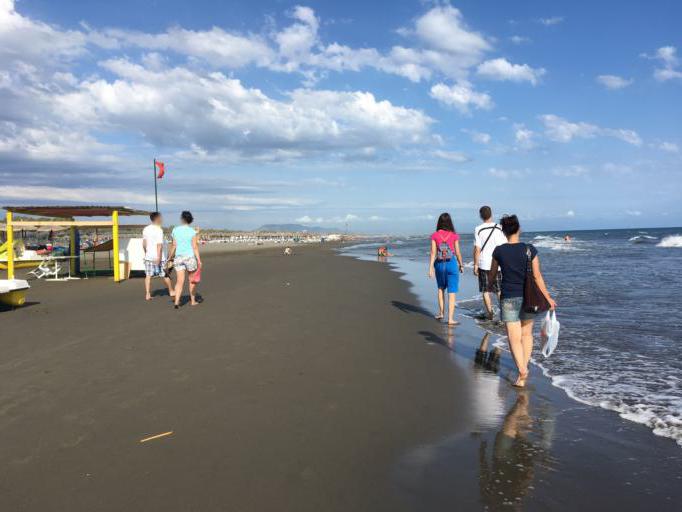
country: ME
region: Ulcinj
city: Ulcinj
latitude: 41.9059
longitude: 19.2529
